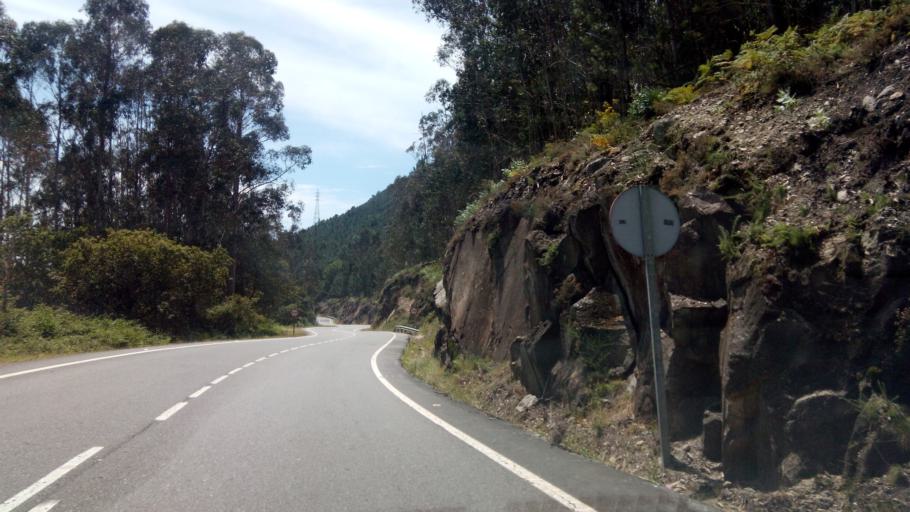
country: ES
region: Galicia
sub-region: Provincia de Pontevedra
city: Moana
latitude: 42.3254
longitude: -8.7218
